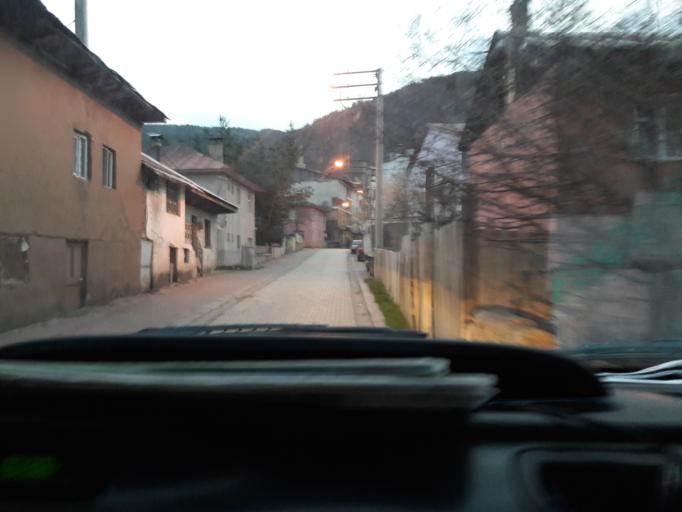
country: TR
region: Giresun
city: Alucra
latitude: 40.3216
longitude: 38.7647
